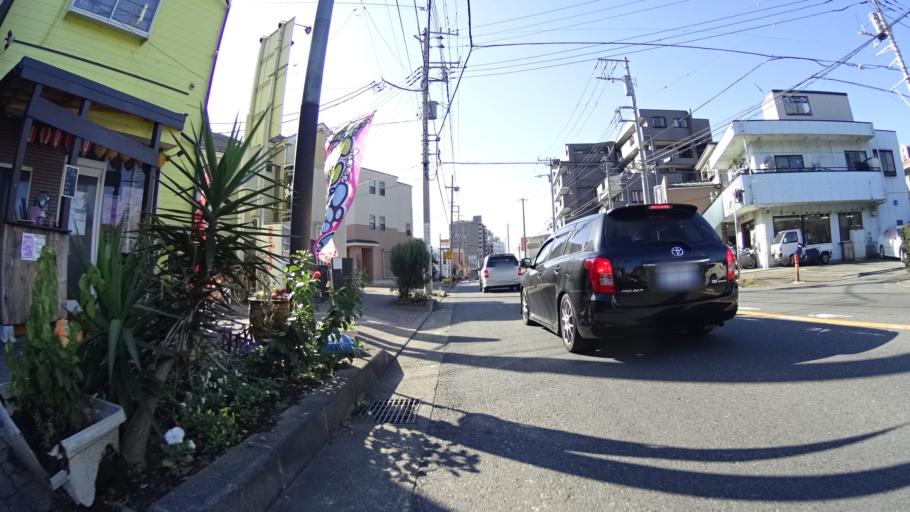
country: JP
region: Kanagawa
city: Zama
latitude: 35.5604
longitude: 139.3585
